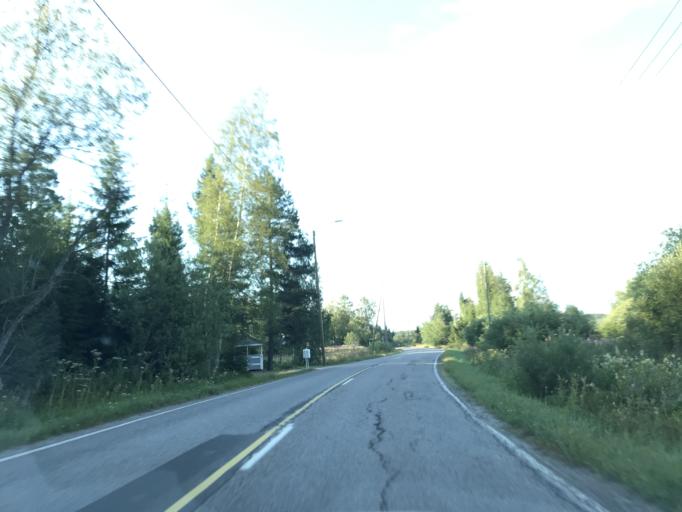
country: FI
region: Uusimaa
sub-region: Helsinki
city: Nurmijaervi
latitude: 60.3693
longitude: 24.6815
